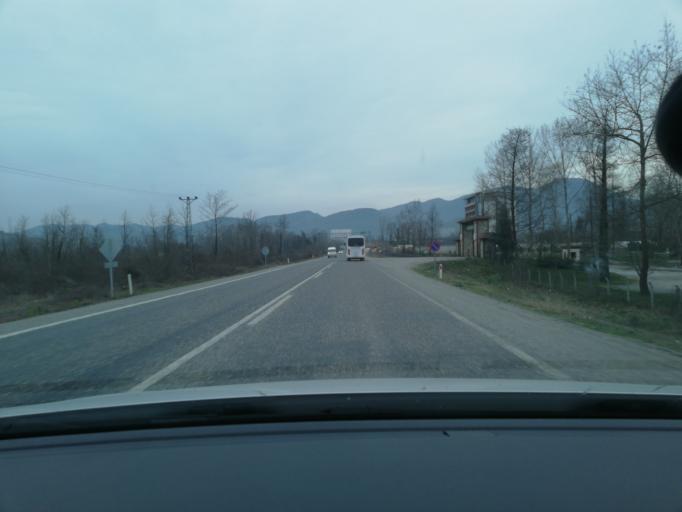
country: TR
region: Zonguldak
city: Gokcebey
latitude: 41.3021
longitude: 32.1071
